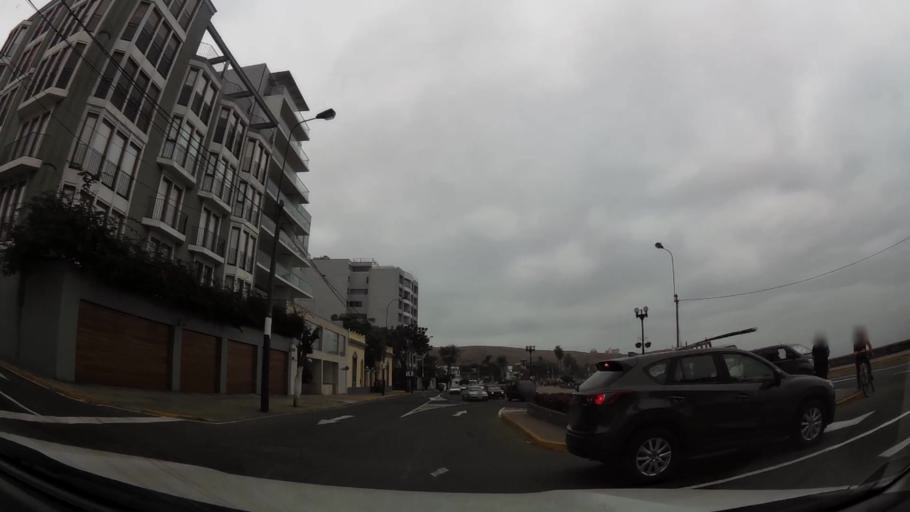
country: PE
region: Lima
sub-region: Lima
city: Surco
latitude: -12.1654
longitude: -77.0256
